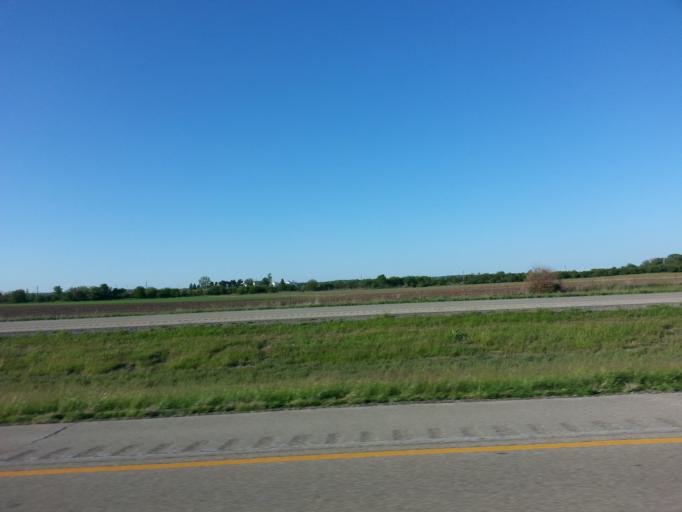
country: US
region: Illinois
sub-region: McLean County
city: Le Roy
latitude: 40.3569
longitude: -88.8044
